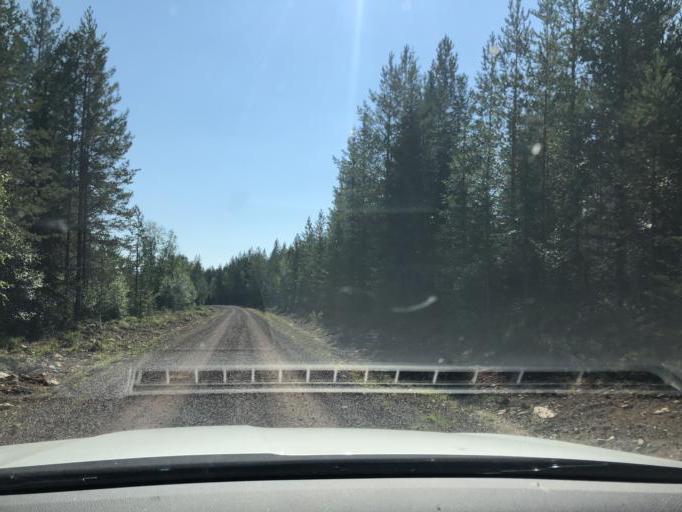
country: SE
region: Dalarna
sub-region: Orsa Kommun
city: Orsa
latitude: 61.2544
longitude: 14.7311
